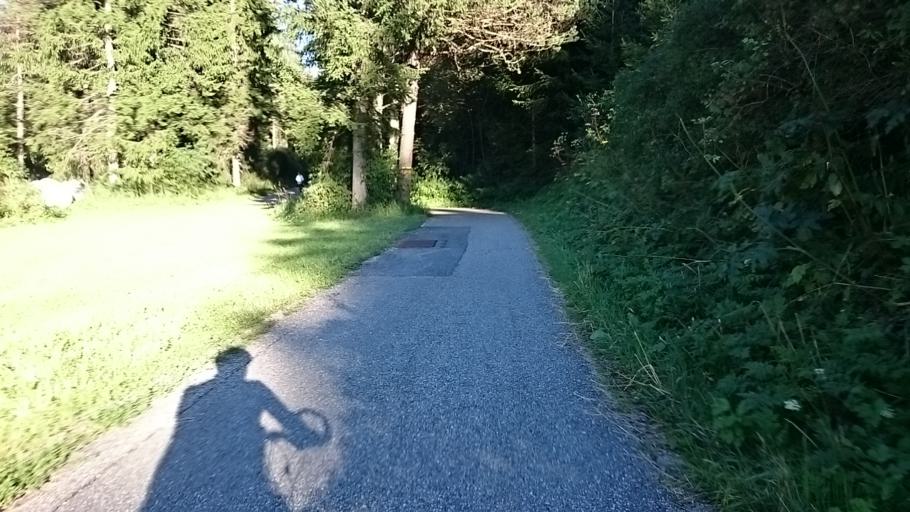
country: IT
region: Trentino-Alto Adige
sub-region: Bolzano
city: Dobbiaco
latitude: 46.7289
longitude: 12.2087
